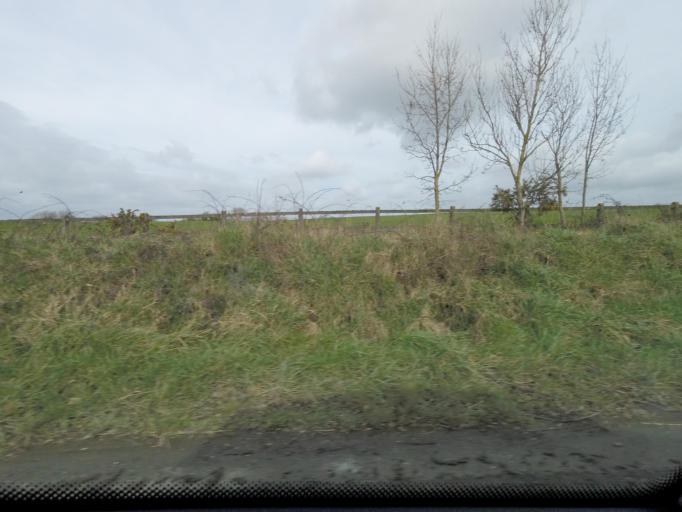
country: IE
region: Leinster
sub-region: Kildare
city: Naas
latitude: 53.2070
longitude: -6.6355
